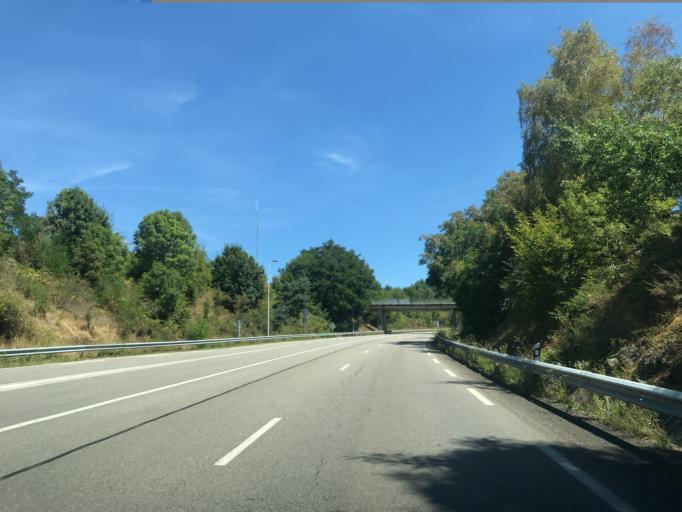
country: FR
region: Limousin
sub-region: Departement de la Correze
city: Tulle
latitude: 45.2786
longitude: 1.7909
